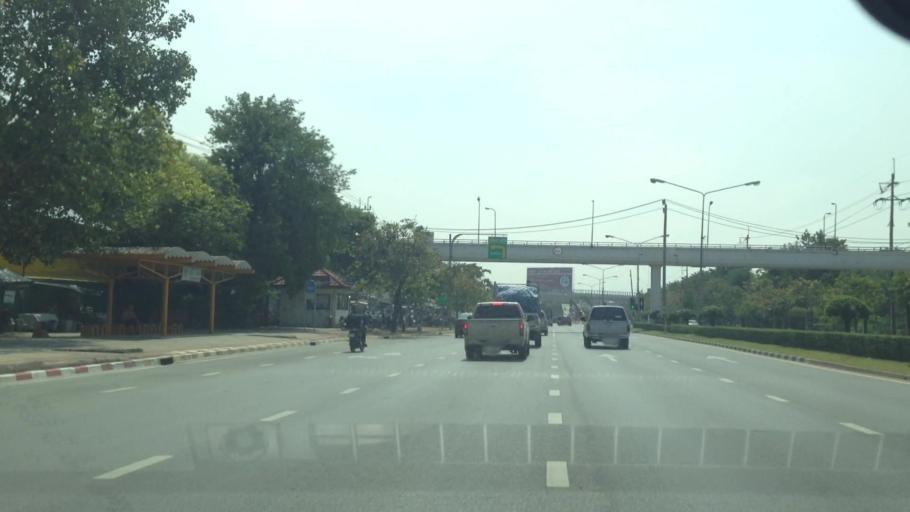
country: TH
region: Bangkok
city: Sai Mai
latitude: 13.9311
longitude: 100.6259
